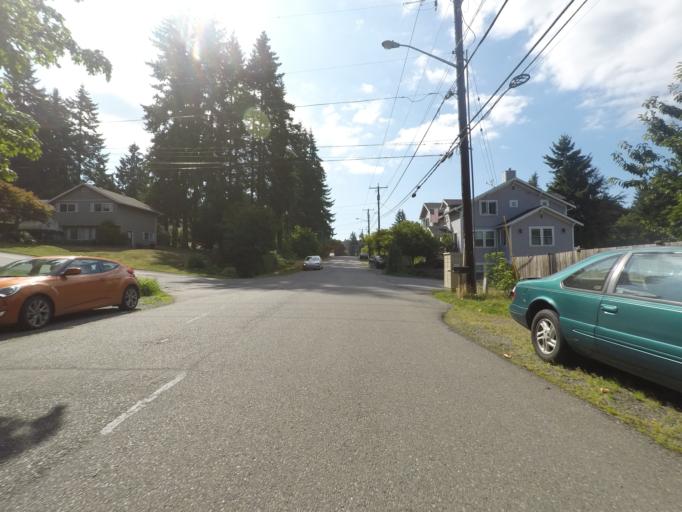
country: US
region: Washington
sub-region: King County
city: Kenmore
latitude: 47.7726
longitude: -122.2559
